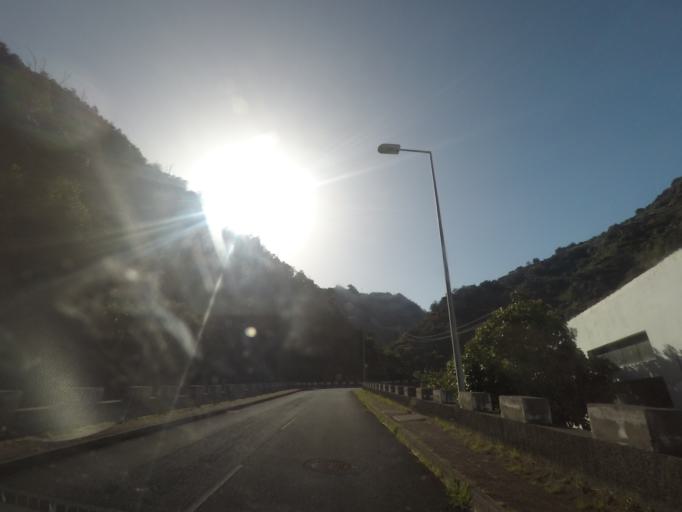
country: PT
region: Madeira
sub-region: Santa Cruz
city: Santa Cruz
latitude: 32.6919
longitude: -16.8004
